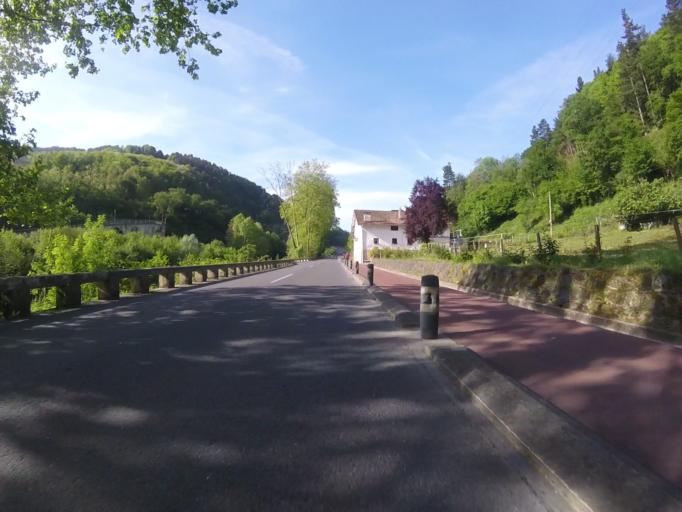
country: ES
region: Basque Country
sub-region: Provincia de Guipuzcoa
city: Legorreta
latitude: 43.0794
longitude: -2.1591
